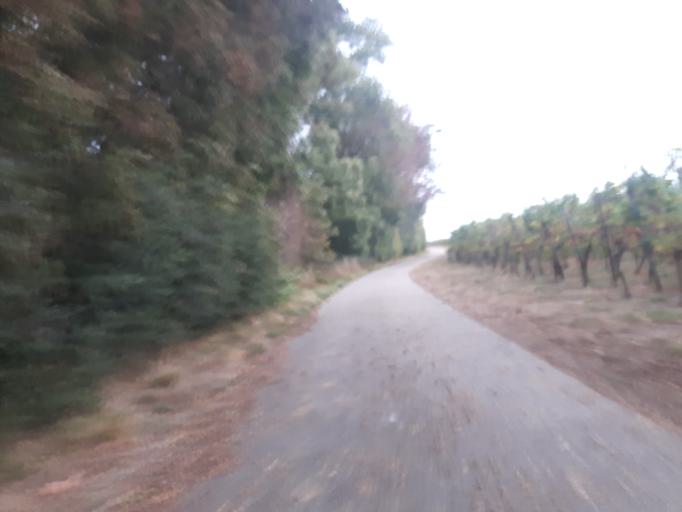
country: DE
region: Baden-Wuerttemberg
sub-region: Regierungsbezirk Stuttgart
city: Flein
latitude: 49.0870
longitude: 9.2105
